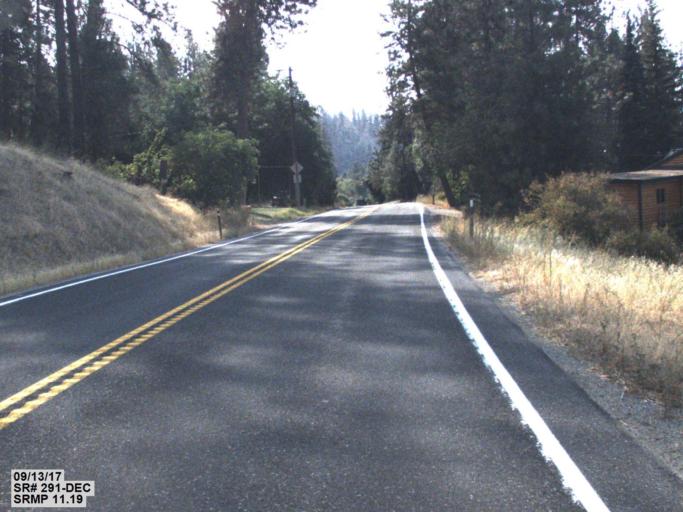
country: US
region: Washington
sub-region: Spokane County
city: Fairwood
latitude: 47.7973
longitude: -117.5349
